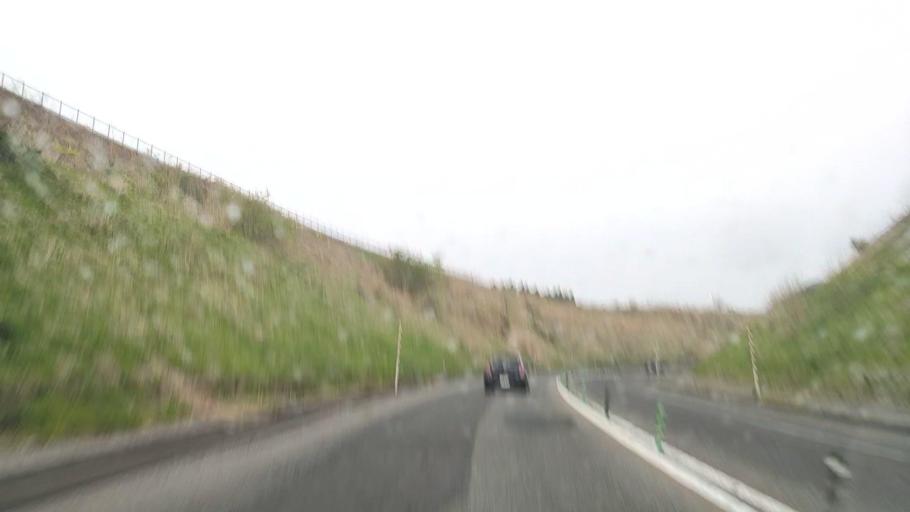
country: JP
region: Akita
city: Noshiromachi
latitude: 40.2090
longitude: 140.1927
